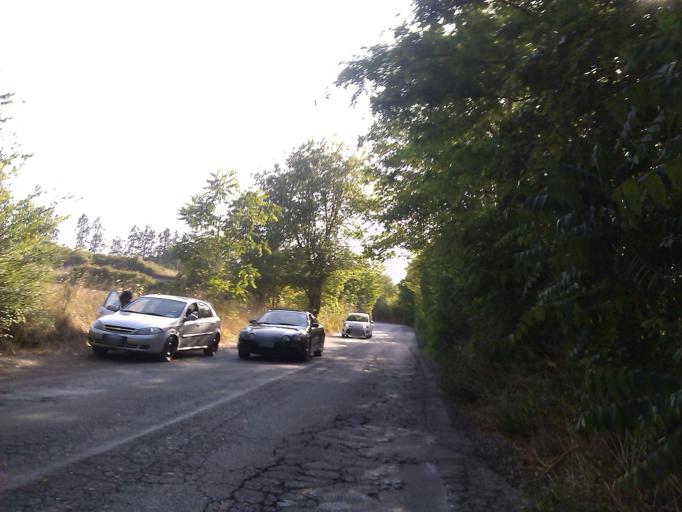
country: IT
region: Latium
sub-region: Citta metropolitana di Roma Capitale
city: Borgo Lotti
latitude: 41.8264
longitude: 12.5314
